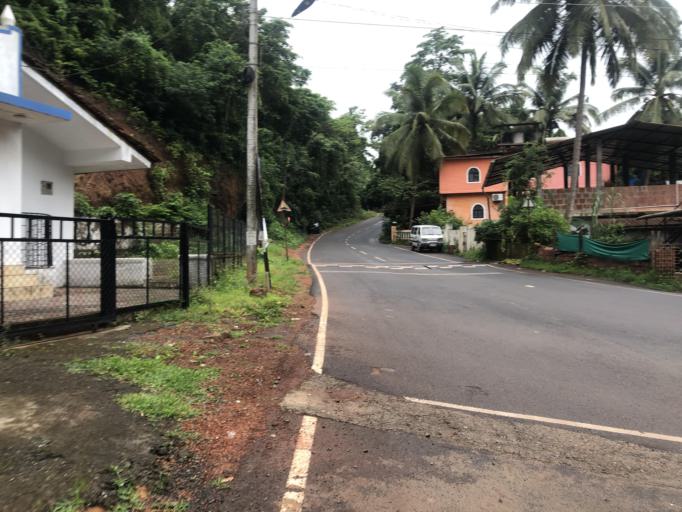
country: IN
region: Goa
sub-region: North Goa
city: Serula
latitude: 15.5430
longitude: 73.8325
